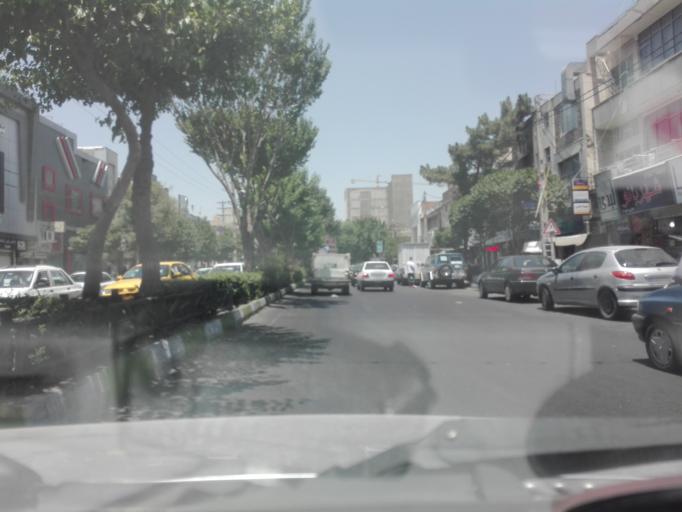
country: IR
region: Tehran
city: Shahre Jadide Andisheh
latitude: 35.7266
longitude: 50.9890
